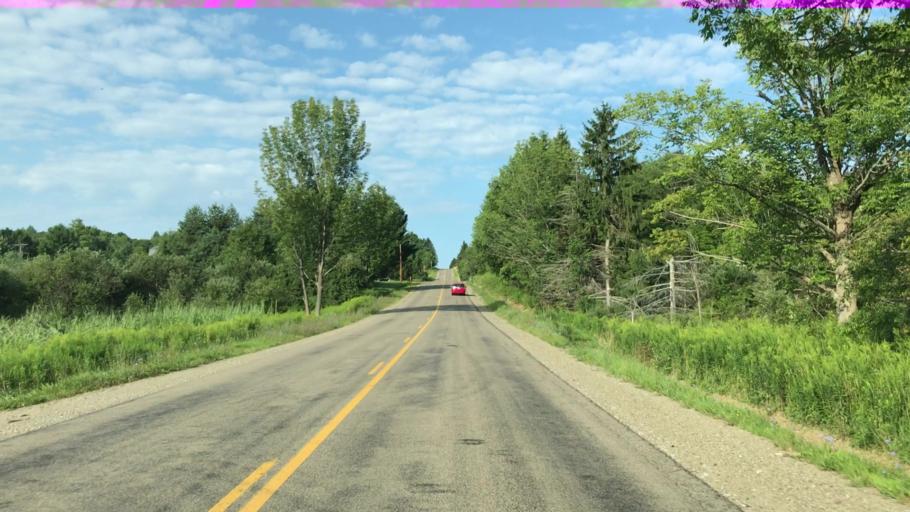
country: US
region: New York
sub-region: Chautauqua County
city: Brocton
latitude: 42.3038
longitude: -79.3894
